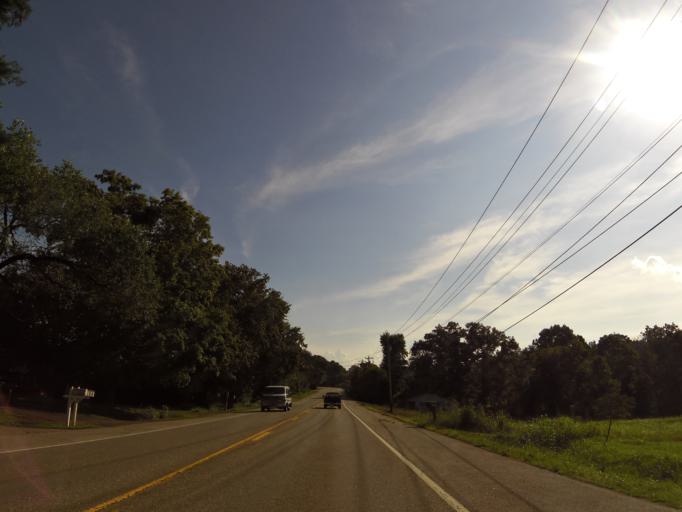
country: US
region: Tennessee
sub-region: Blount County
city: Louisville
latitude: 35.8333
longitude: -84.0134
